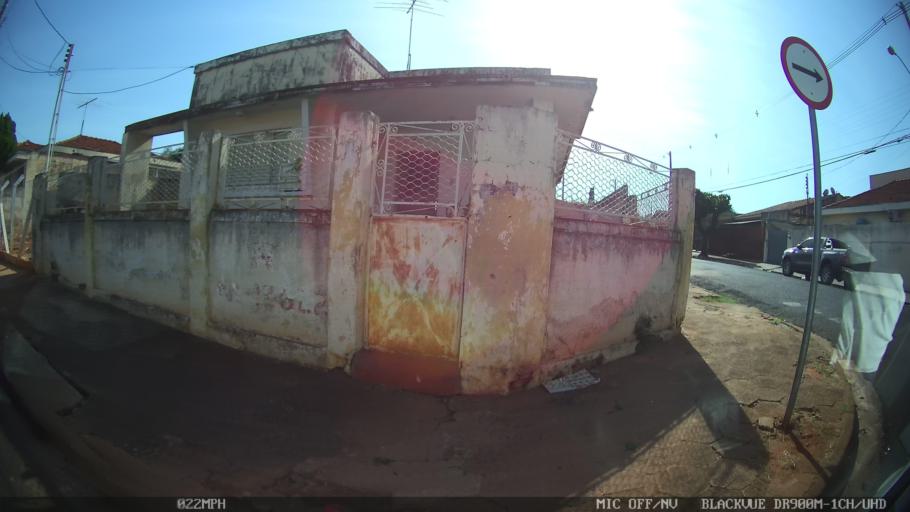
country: BR
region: Sao Paulo
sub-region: Sao Jose Do Rio Preto
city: Sao Jose do Rio Preto
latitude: -20.8010
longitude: -49.3835
